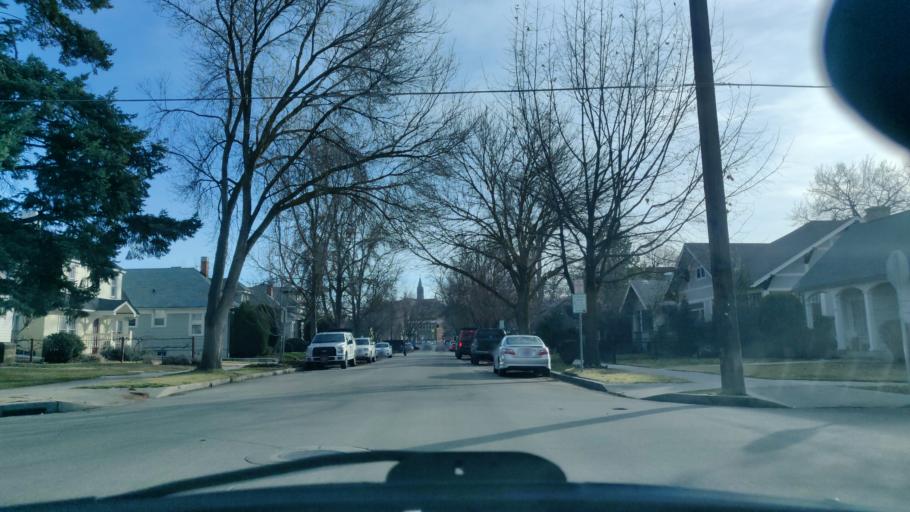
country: US
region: Idaho
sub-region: Ada County
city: Boise
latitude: 43.6249
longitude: -116.1987
